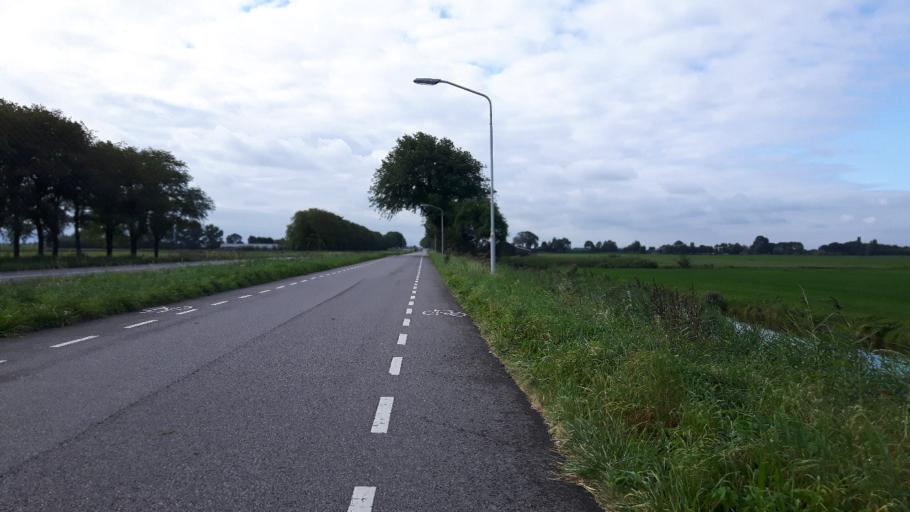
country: NL
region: North Holland
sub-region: Gemeente Hoorn
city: Hoorn
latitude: 52.5986
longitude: 5.0026
